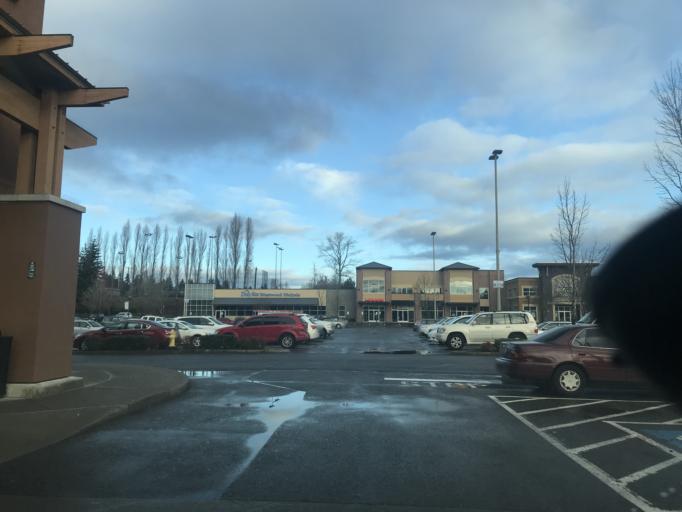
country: US
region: Washington
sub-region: King County
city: White Center
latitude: 47.5233
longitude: -122.3658
